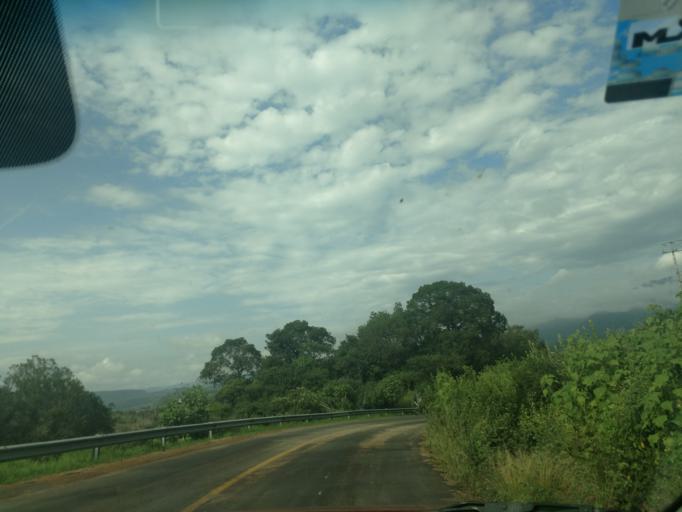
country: MX
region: Jalisco
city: El Salto
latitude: 20.4322
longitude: -104.4791
